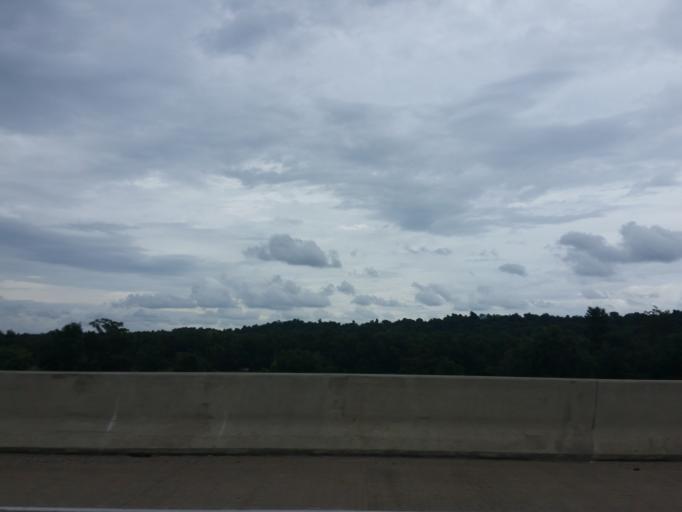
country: US
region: Kentucky
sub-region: Ballard County
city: Wickliffe
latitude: 36.9789
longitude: -89.1008
